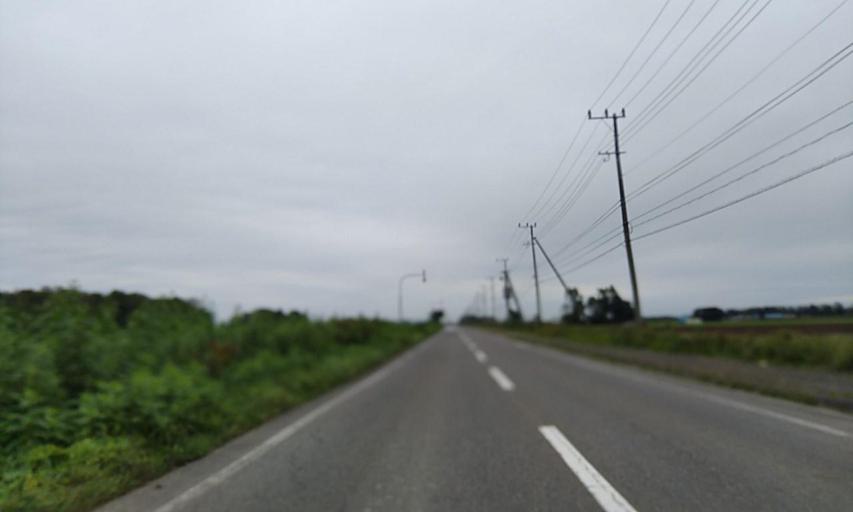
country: JP
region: Hokkaido
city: Obihiro
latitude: 42.6588
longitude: 143.1064
